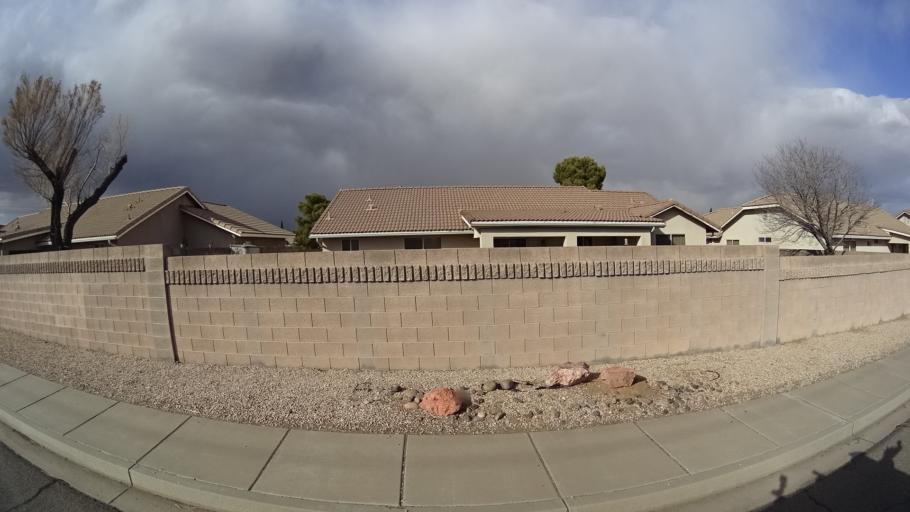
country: US
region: Arizona
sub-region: Mohave County
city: New Kingman-Butler
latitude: 35.2321
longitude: -114.0323
